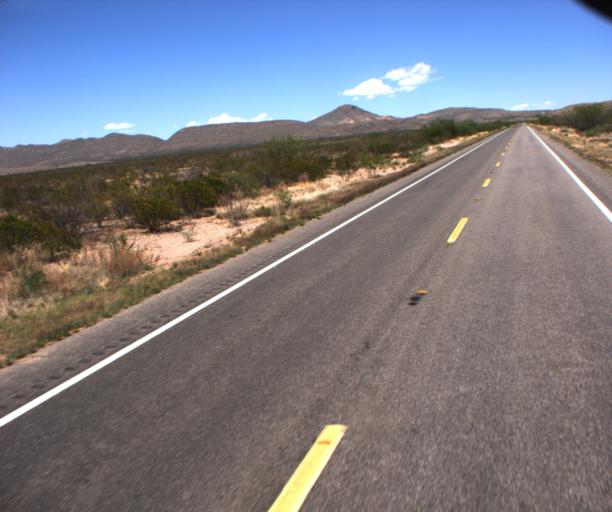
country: US
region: Arizona
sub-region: Cochise County
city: Tombstone
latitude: 31.6253
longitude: -110.0490
